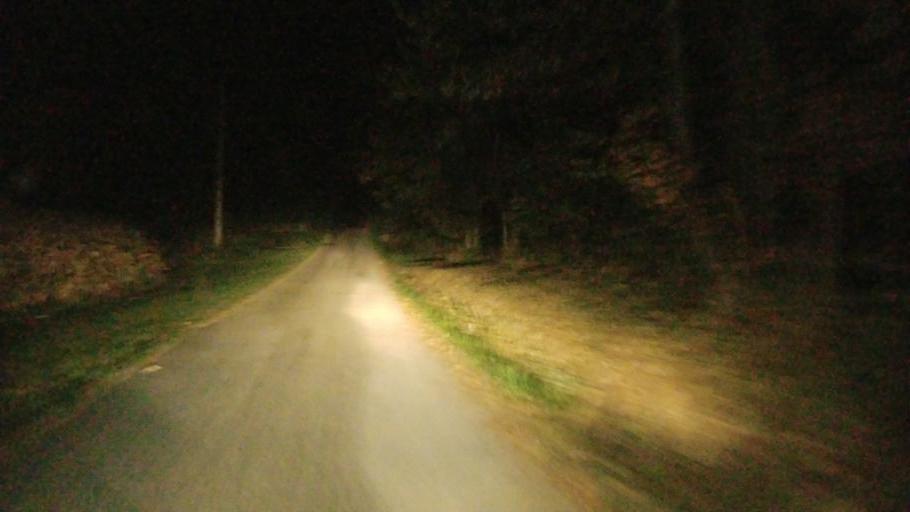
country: US
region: Ohio
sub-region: Ashland County
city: Loudonville
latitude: 40.7046
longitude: -82.2215
